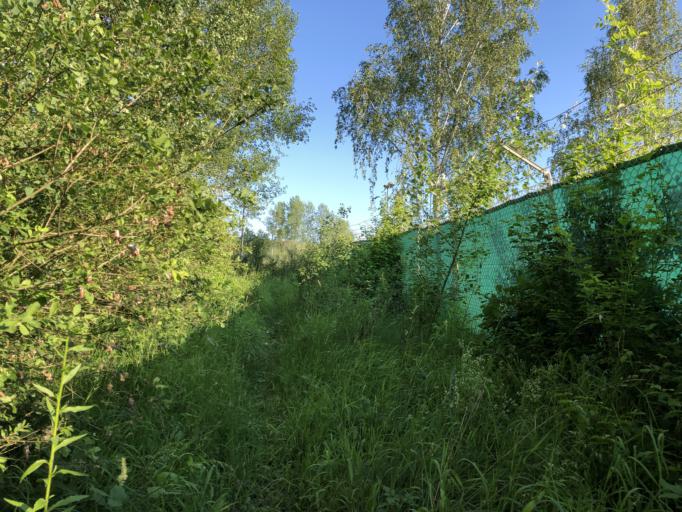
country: DE
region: Bavaria
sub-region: Upper Franconia
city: Memmelsdorf
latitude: 49.9170
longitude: 10.9460
